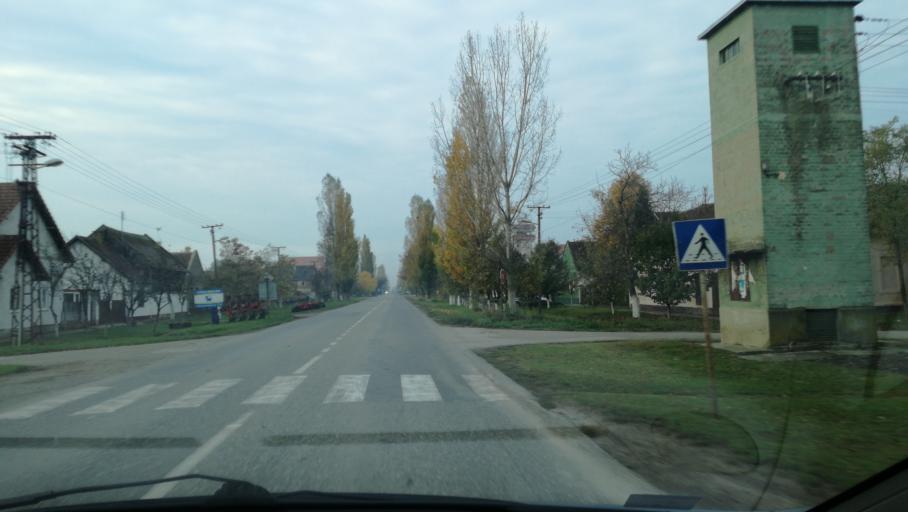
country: RS
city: Basaid
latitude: 45.6459
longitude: 20.4175
